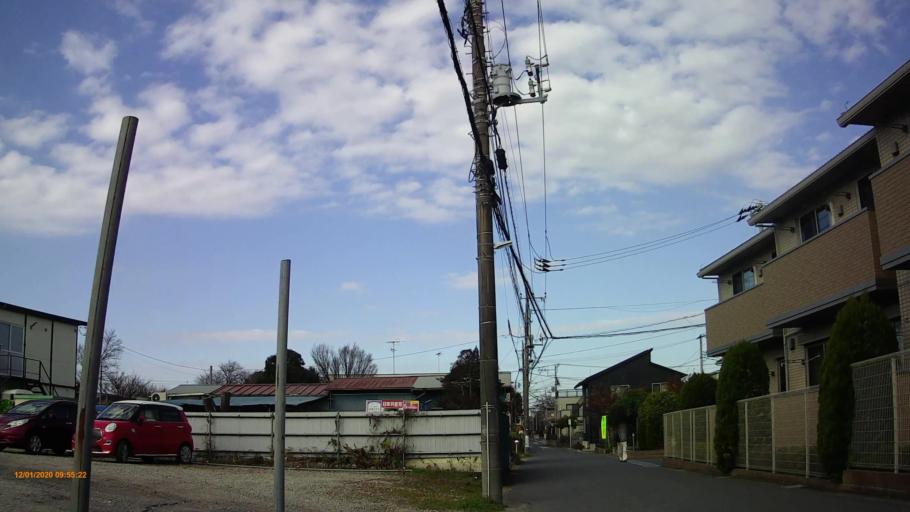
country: JP
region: Chiba
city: Yotsukaido
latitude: 35.6299
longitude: 140.1830
